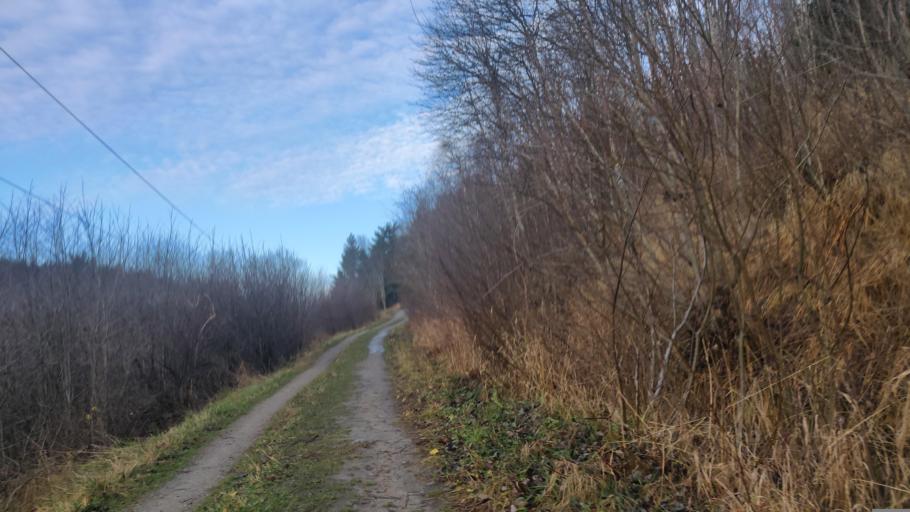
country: SE
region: Vaesternorrland
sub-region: Sundsvalls Kommun
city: Nolby
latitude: 62.3001
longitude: 17.3571
